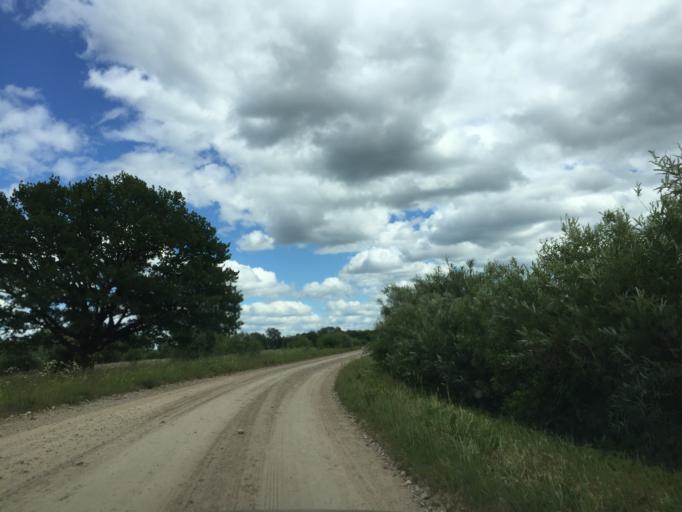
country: LV
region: Lecava
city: Iecava
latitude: 56.5886
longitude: 24.2422
